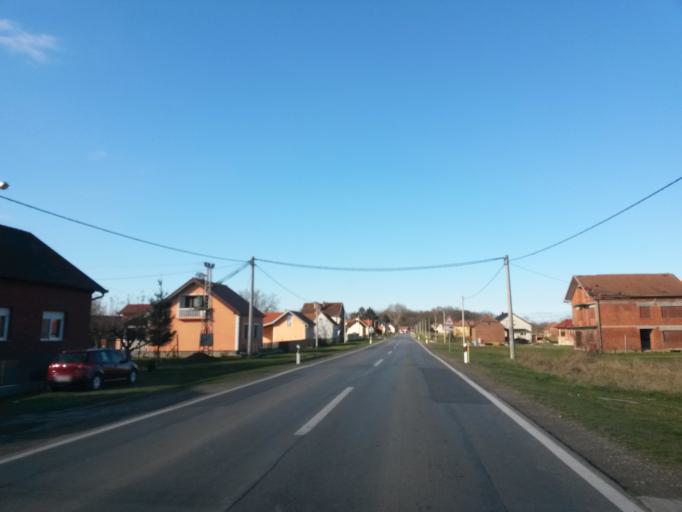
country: HR
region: Virovitick-Podravska
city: Suhopolje
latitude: 45.7945
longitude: 17.5075
